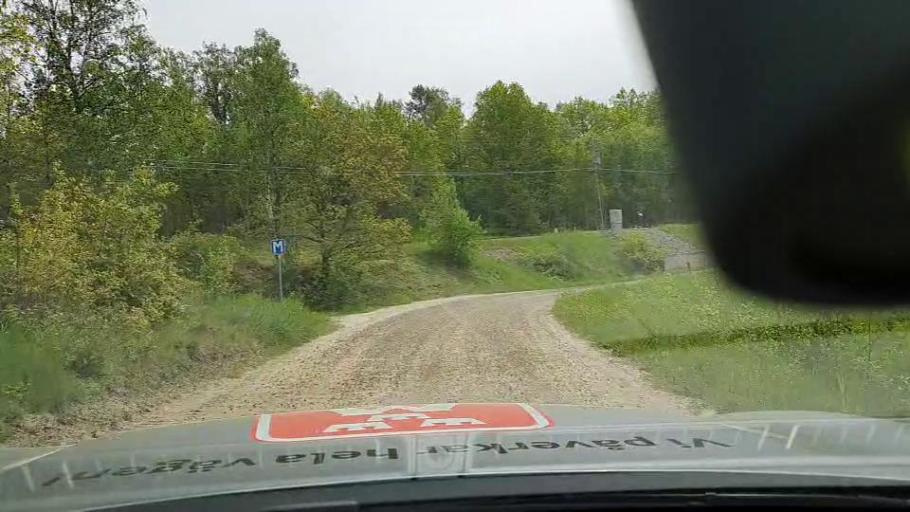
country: SE
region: Soedermanland
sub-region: Flens Kommun
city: Flen
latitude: 59.0403
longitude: 16.5801
